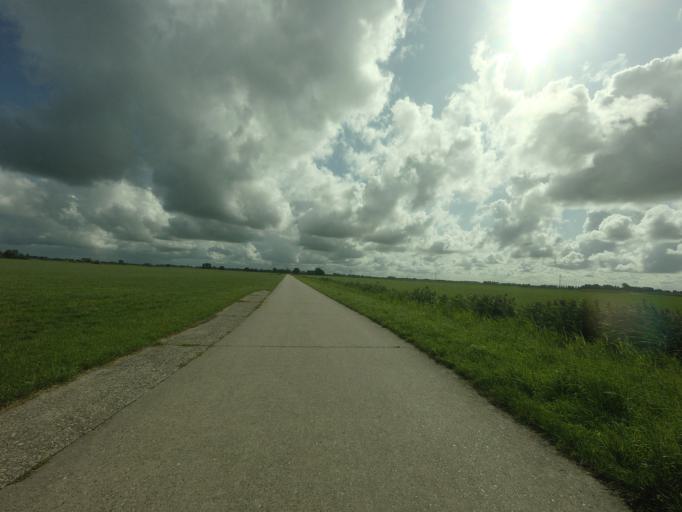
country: NL
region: Friesland
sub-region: Sudwest Fryslan
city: Scharnegoutum
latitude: 53.0706
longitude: 5.6372
